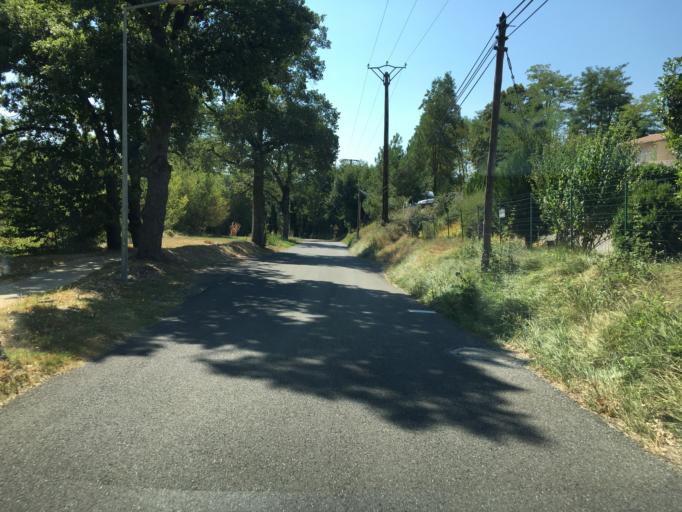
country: FR
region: Provence-Alpes-Cote d'Azur
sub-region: Departement des Alpes-de-Haute-Provence
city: Mallemoisson
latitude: 44.0605
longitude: 6.1482
